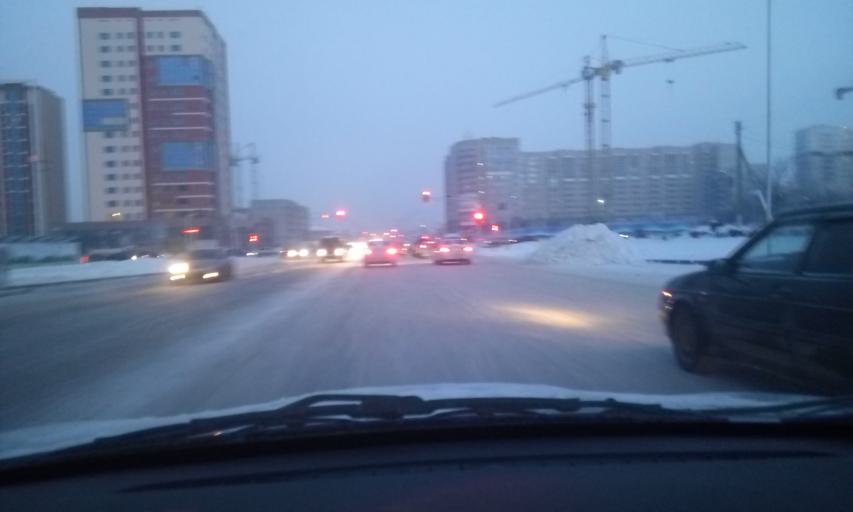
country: KZ
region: Astana Qalasy
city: Astana
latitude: 51.1281
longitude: 71.4978
